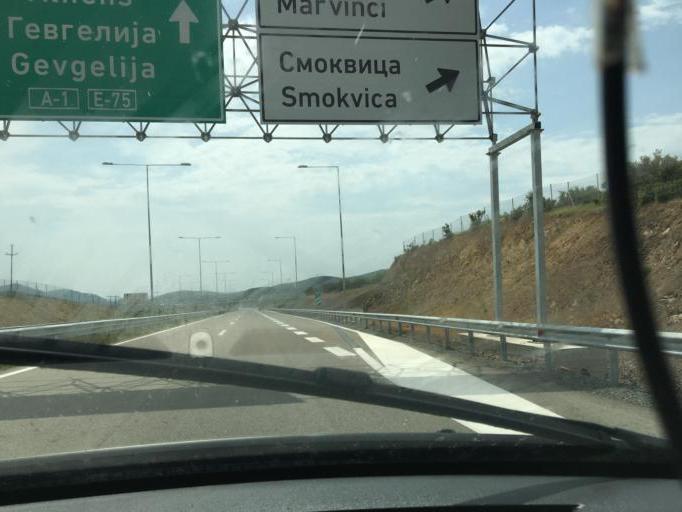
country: MK
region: Gevgelija
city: Miravci
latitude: 41.2676
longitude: 22.4685
